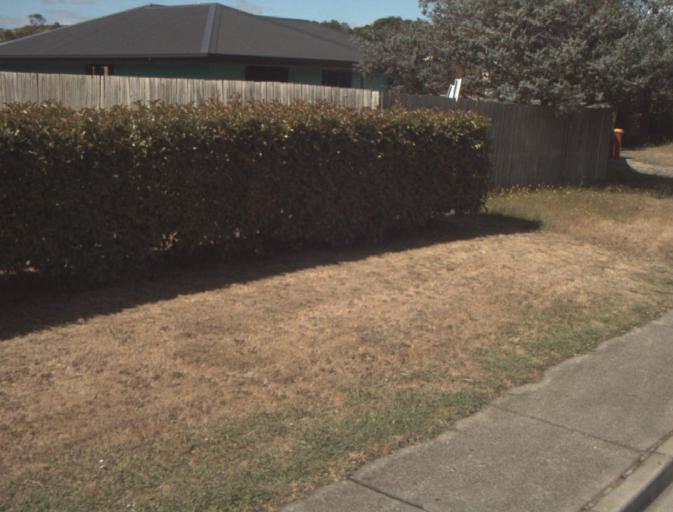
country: AU
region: Tasmania
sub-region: Launceston
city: Newstead
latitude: -41.4182
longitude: 147.1836
